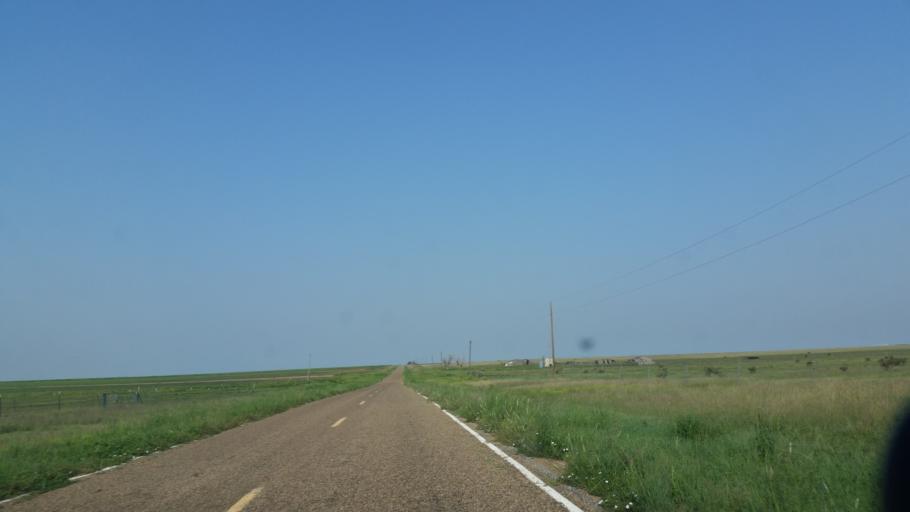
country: US
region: New Mexico
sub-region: Quay County
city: Logan
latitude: 34.9229
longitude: -103.2648
